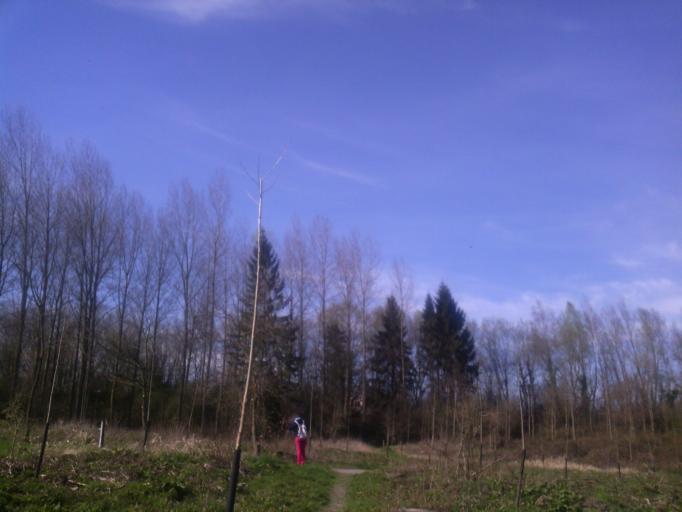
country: BE
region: Wallonia
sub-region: Province du Hainaut
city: Silly
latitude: 50.6706
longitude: 3.9225
